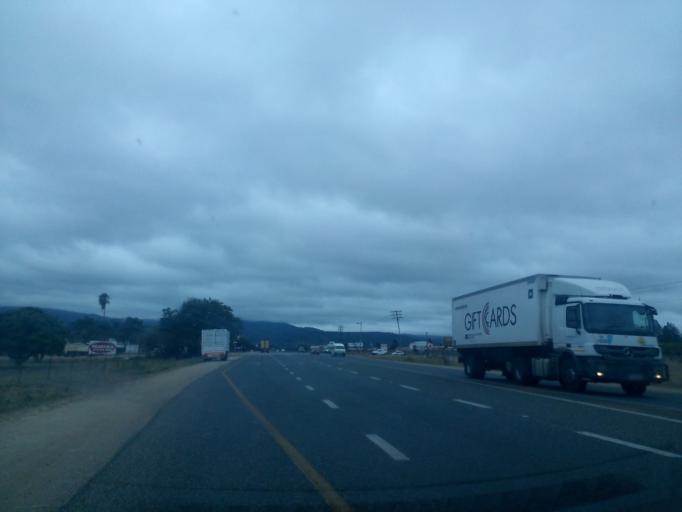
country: ZA
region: Limpopo
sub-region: Vhembe District Municipality
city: Louis Trichardt
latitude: -23.0710
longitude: 29.9110
